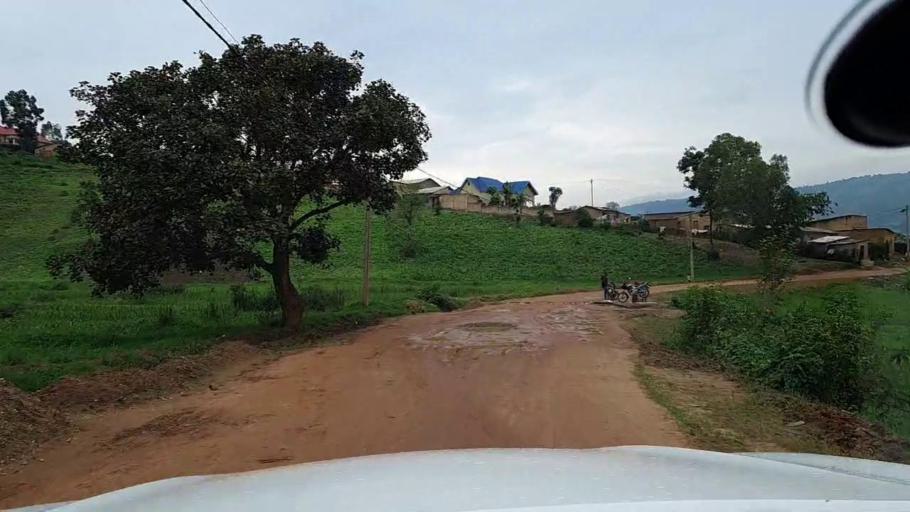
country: RW
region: Kigali
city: Kigali
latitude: -1.9621
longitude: 29.9960
